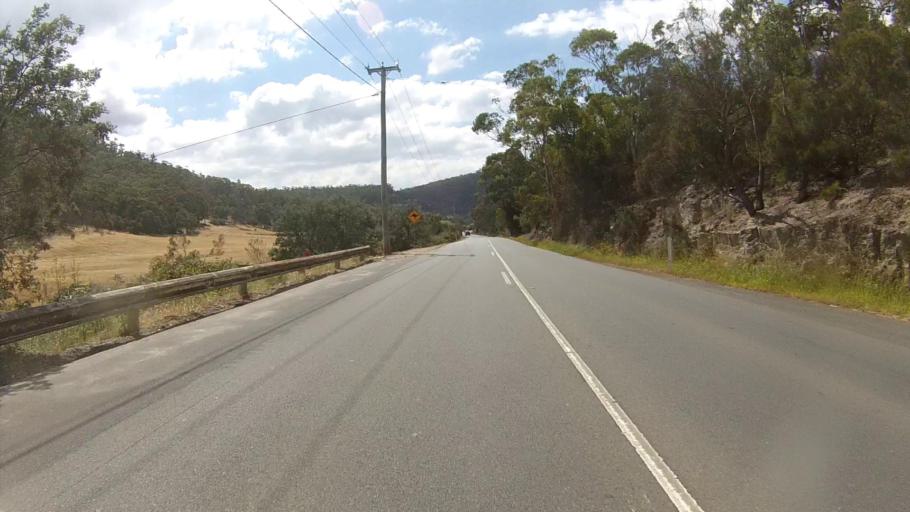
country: AU
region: Tasmania
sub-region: Clarence
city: Cambridge
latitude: -42.8442
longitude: 147.4201
